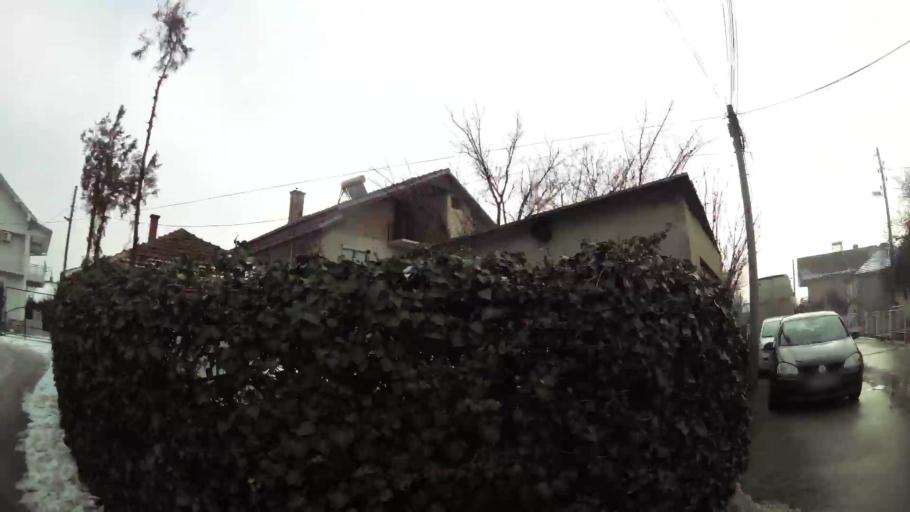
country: MK
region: Ilinden
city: Marino
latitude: 41.9958
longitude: 21.5870
